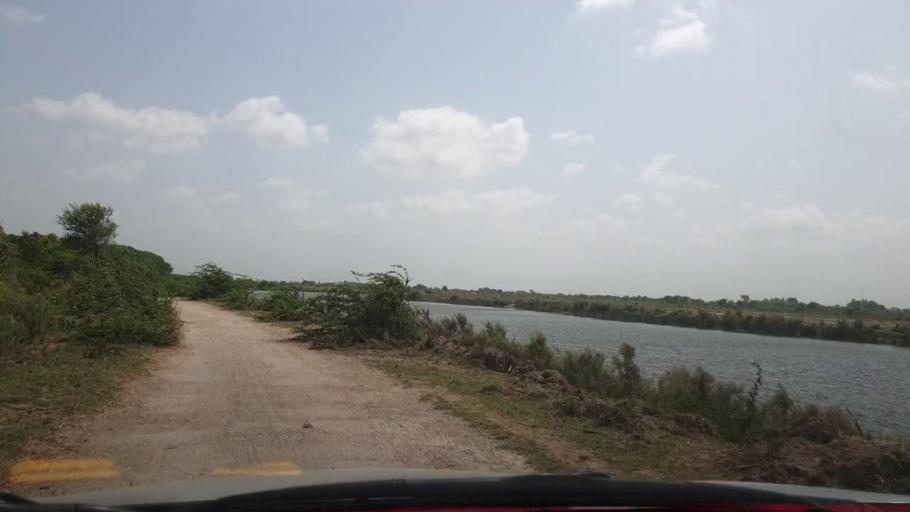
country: PK
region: Sindh
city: Tando Bago
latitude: 24.8694
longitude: 68.9171
